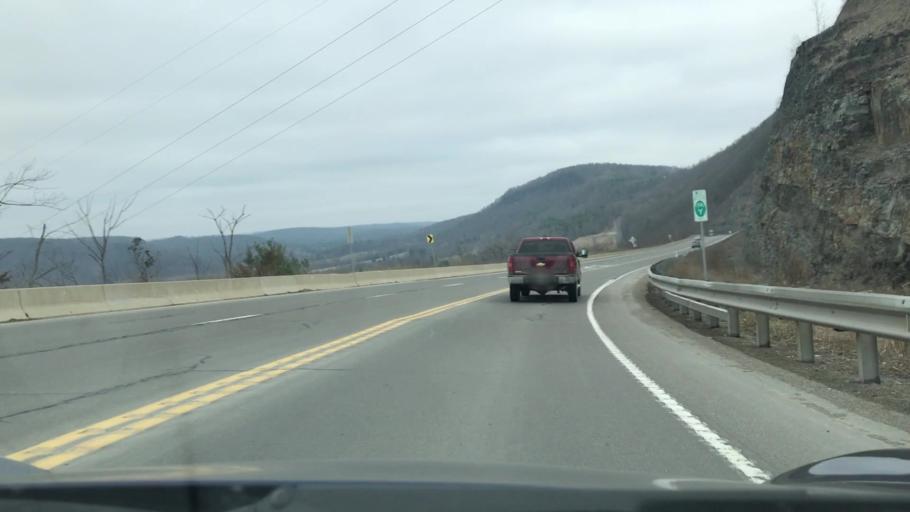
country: US
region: Pennsylvania
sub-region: Bradford County
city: Towanda
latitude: 41.7620
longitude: -76.3698
